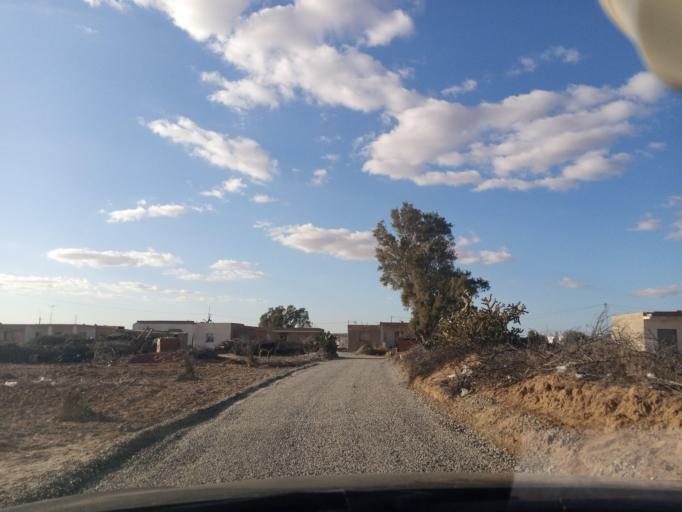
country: TN
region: Safaqis
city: Bi'r `Ali Bin Khalifah
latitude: 34.7100
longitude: 10.4247
